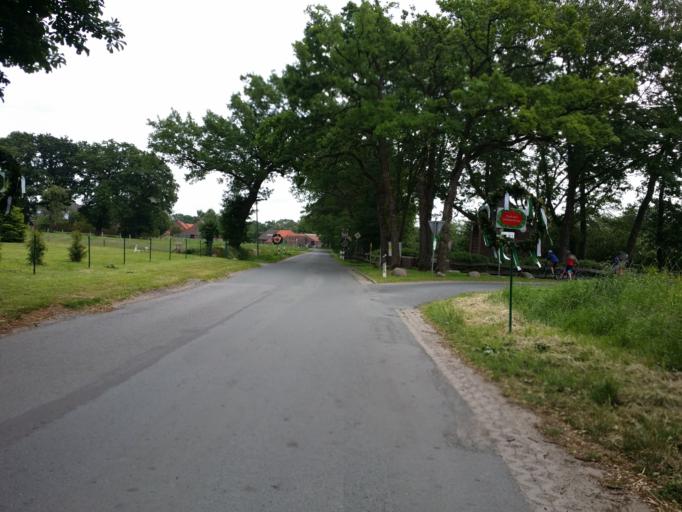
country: DE
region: Lower Saxony
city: Friedeburg
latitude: 53.4658
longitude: 7.8328
